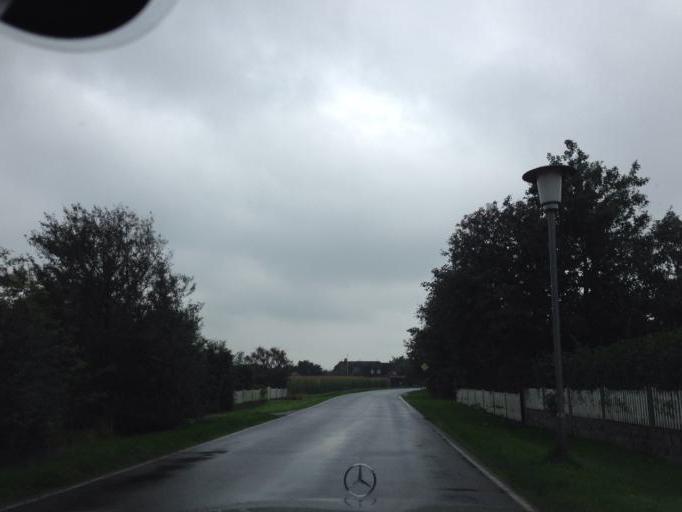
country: DE
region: Schleswig-Holstein
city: Dunsum
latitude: 54.7309
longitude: 8.4144
